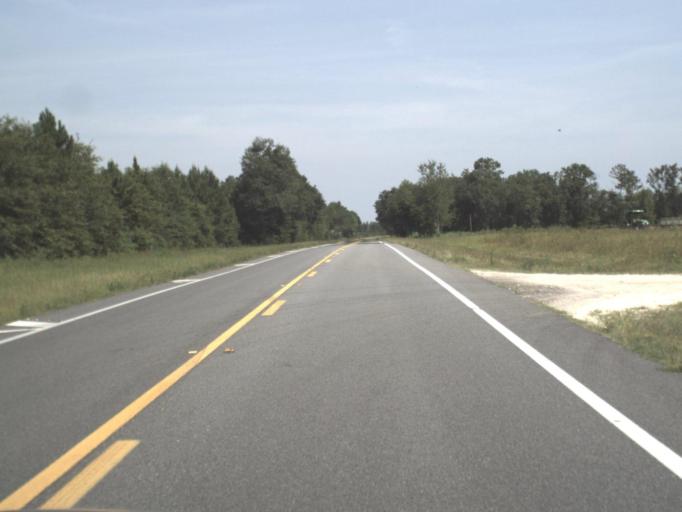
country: US
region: Georgia
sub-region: Echols County
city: Statenville
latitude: 30.6056
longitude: -83.0178
